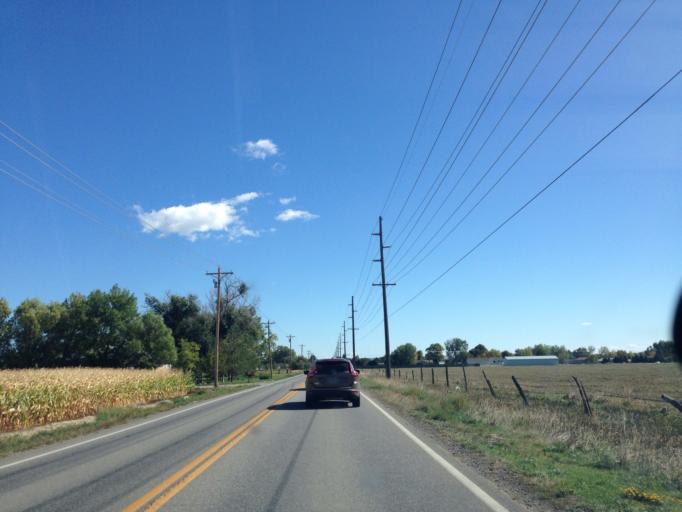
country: US
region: Montana
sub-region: Yellowstone County
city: Billings
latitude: 45.7841
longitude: -108.6446
